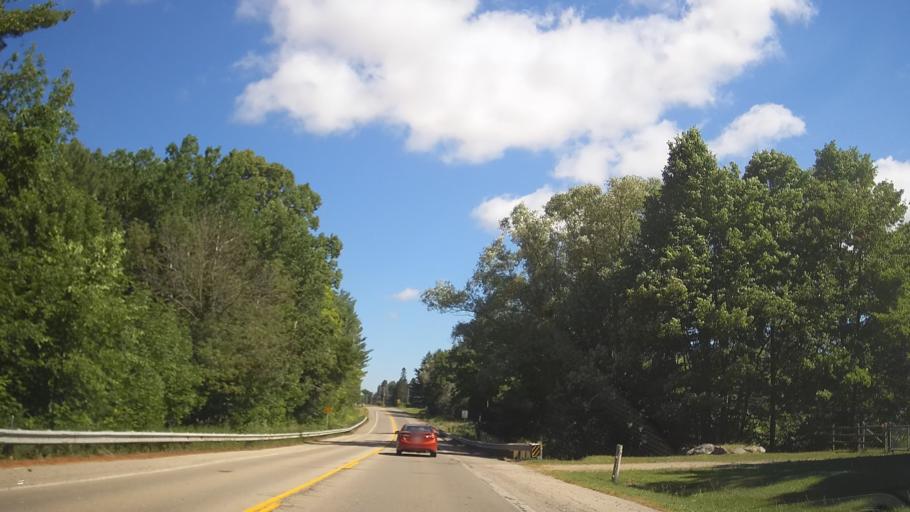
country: US
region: Michigan
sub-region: Cheboygan County
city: Indian River
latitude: 45.4678
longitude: -84.7813
